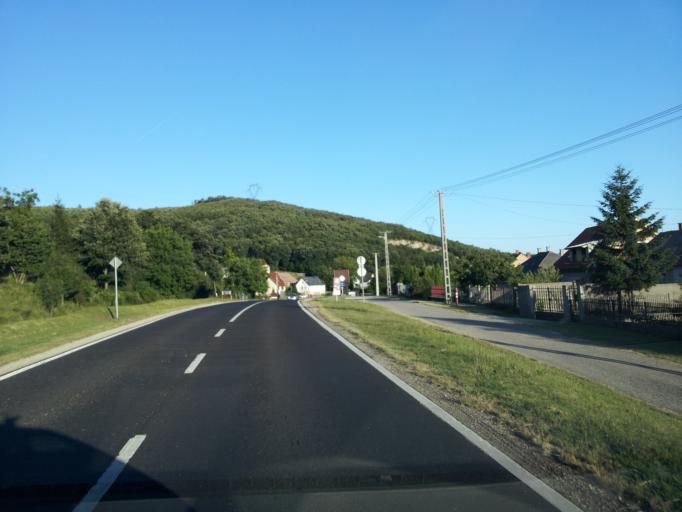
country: HU
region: Veszprem
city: Zirc
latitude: 47.2069
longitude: 17.9190
